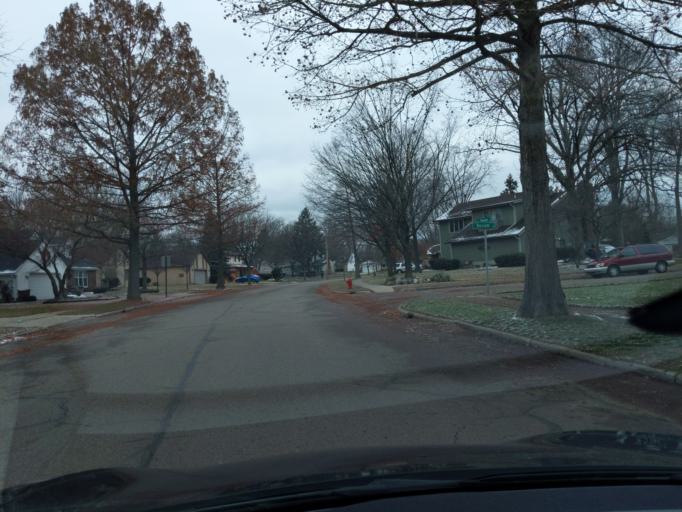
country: US
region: Michigan
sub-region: Ingham County
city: East Lansing
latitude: 42.7544
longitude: -84.5114
